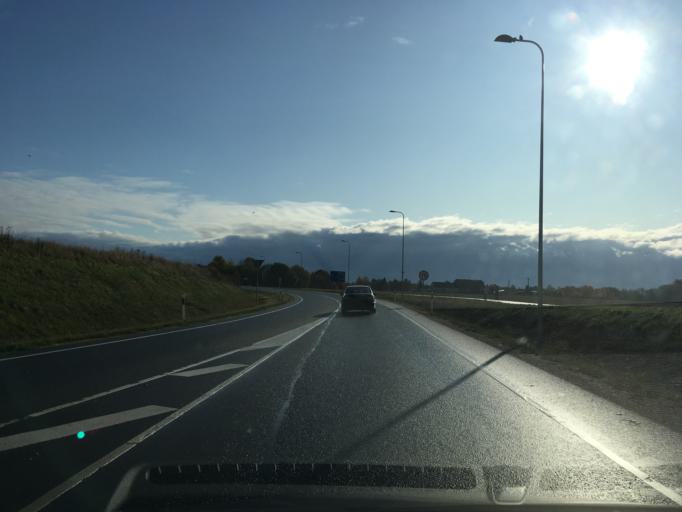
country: EE
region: Harju
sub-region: Rae vald
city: Vaida
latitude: 59.1824
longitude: 25.1123
